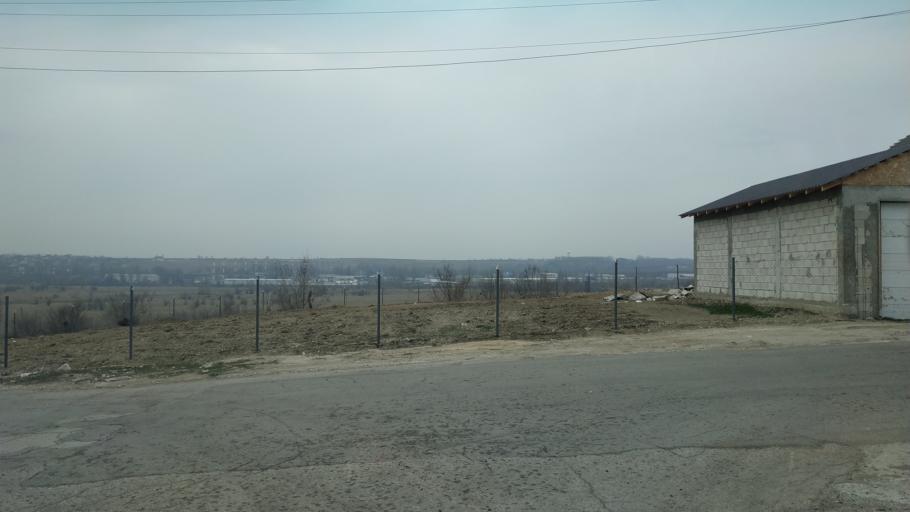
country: MD
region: Chisinau
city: Singera
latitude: 46.9347
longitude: 28.9782
